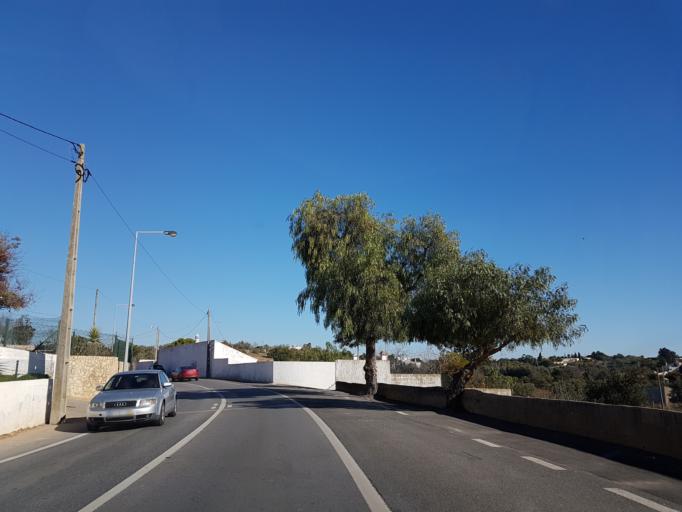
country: PT
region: Faro
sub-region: Lagoa
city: Carvoeiro
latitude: 37.1118
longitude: -8.4558
